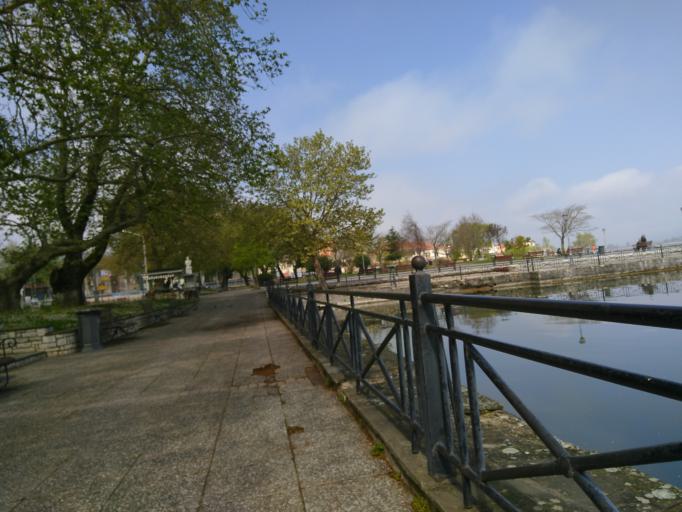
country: GR
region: Epirus
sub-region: Nomos Ioanninon
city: Ioannina
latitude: 39.6728
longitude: 20.8561
